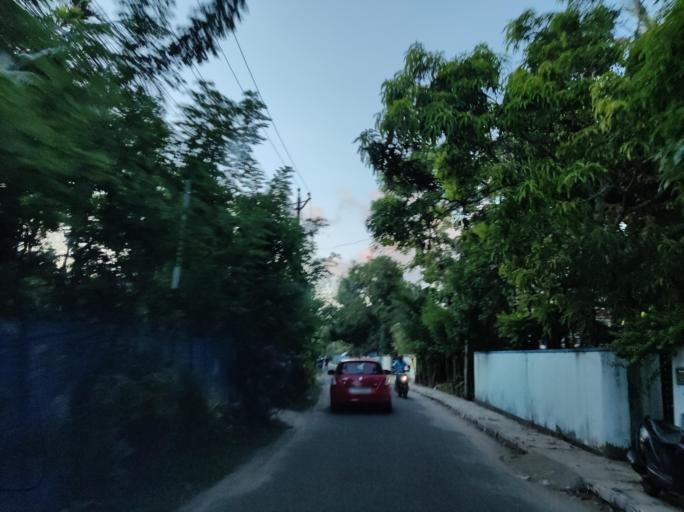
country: IN
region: Kerala
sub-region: Alappuzha
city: Vayalar
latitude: 9.7396
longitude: 76.2885
